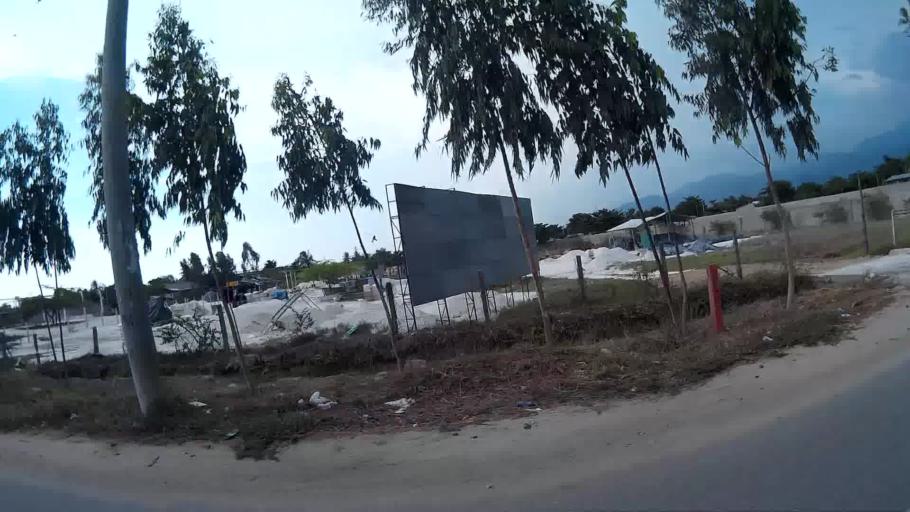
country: CO
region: Magdalena
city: Cienaga
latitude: 11.0048
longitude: -74.2335
